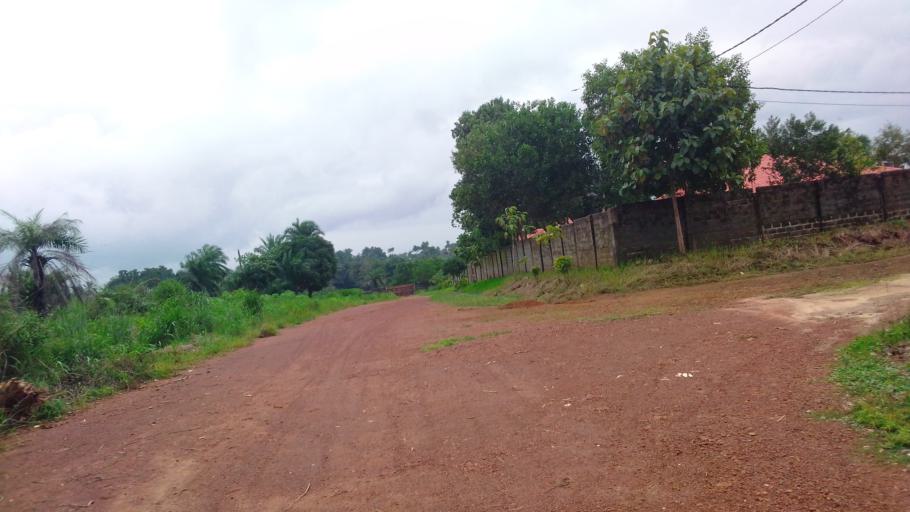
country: SL
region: Northern Province
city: Lunsar
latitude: 8.6942
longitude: -12.5497
